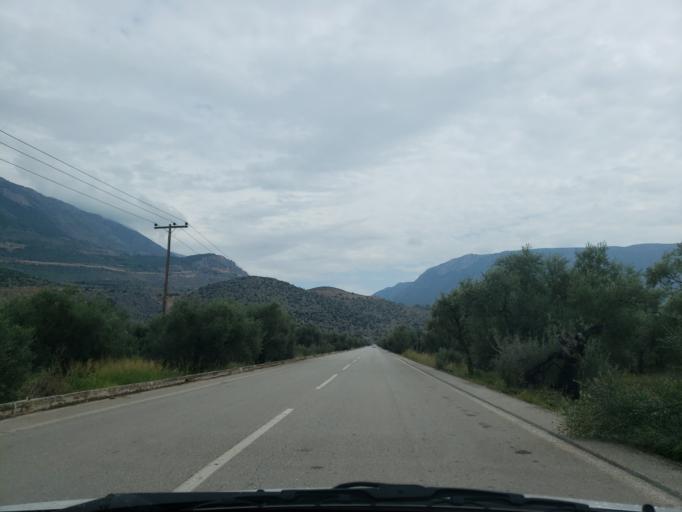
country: GR
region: Central Greece
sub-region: Nomos Fokidos
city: Kirra
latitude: 38.4792
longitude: 22.4431
